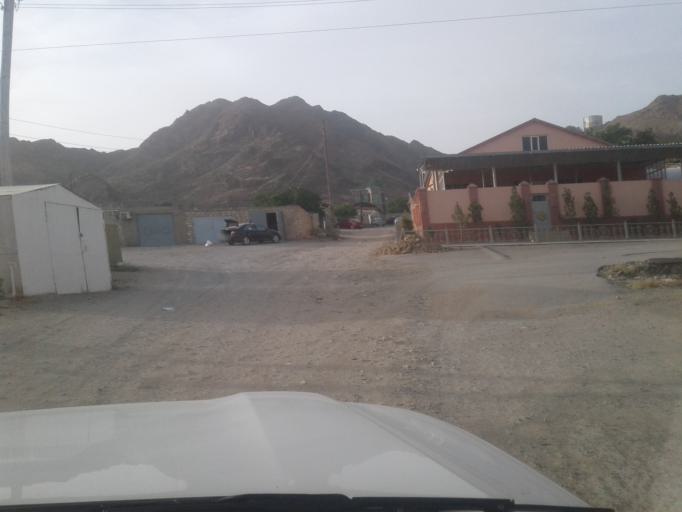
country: TM
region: Balkan
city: Turkmenbasy
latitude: 40.0059
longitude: 52.9651
